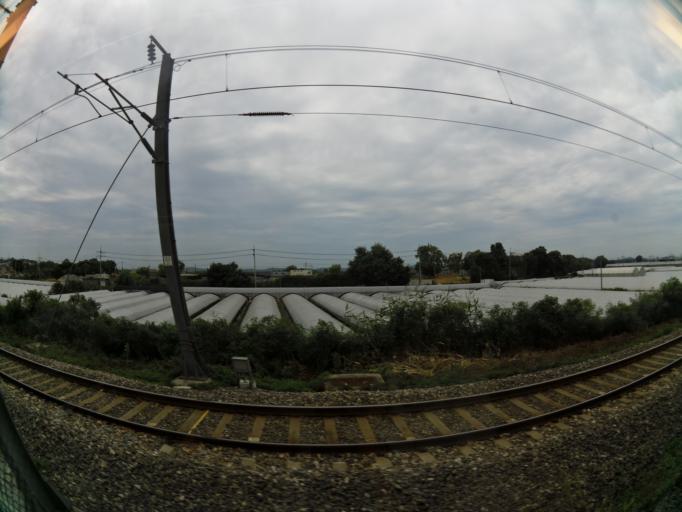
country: KR
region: Gyeonggi-do
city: Osan
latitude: 37.0940
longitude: 127.0599
